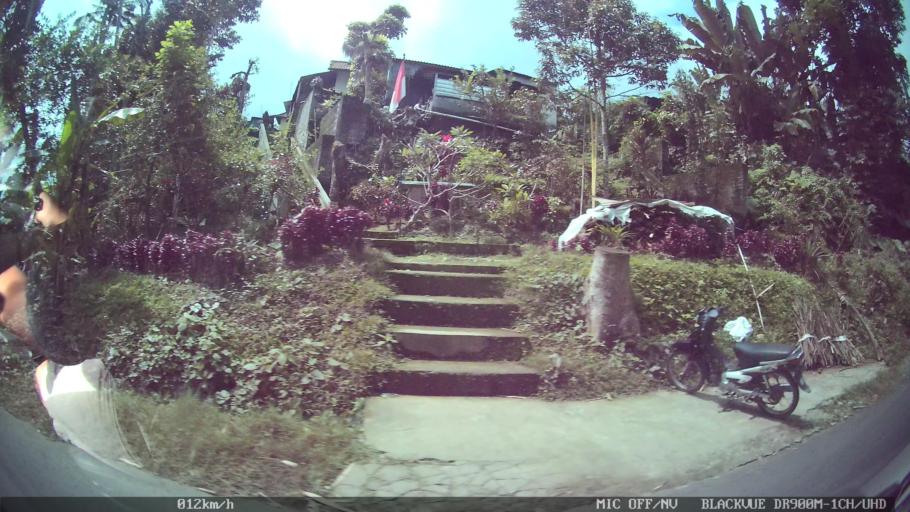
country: ID
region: Bali
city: Banjar Susut Kaja
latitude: -8.4421
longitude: 115.3335
